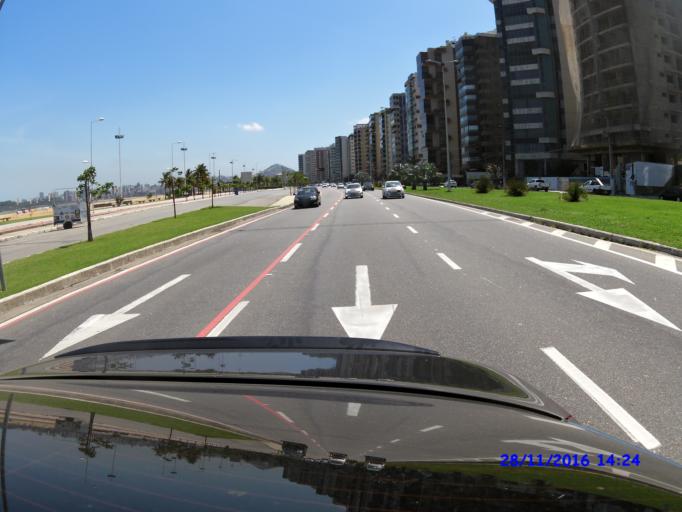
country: BR
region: Espirito Santo
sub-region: Vila Velha
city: Vila Velha
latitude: -20.2758
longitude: -40.2836
